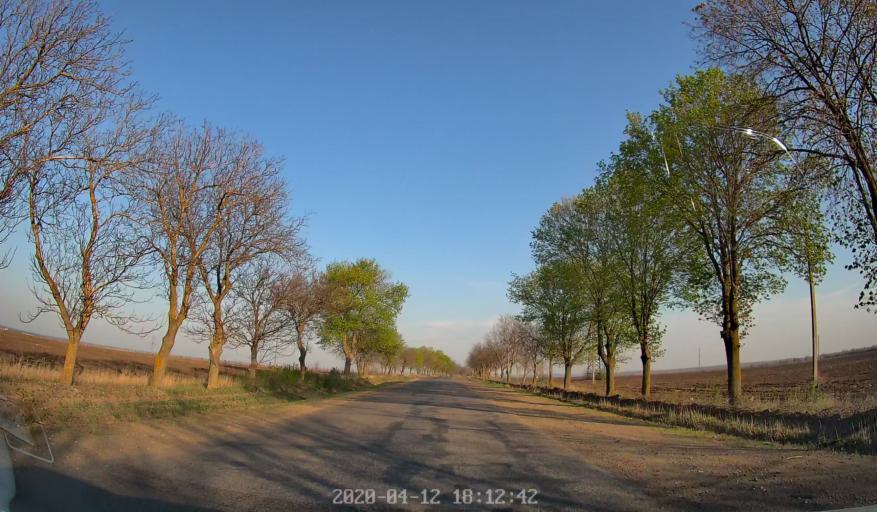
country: MD
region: Telenesti
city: Cocieri
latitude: 47.2743
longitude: 29.1070
